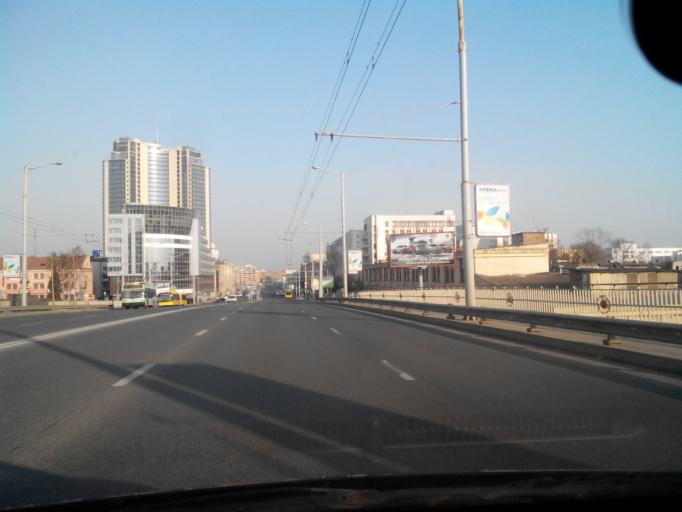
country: BY
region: Minsk
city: Minsk
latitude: 53.9067
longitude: 27.5256
